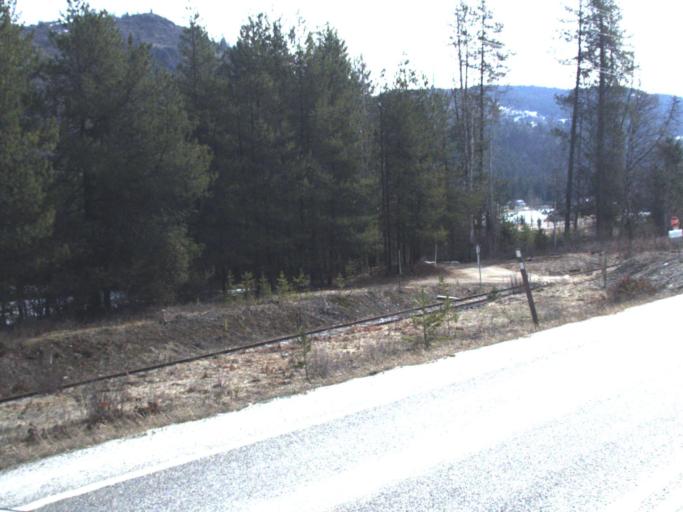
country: CA
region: British Columbia
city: Fruitvale
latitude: 48.6474
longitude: -117.3788
